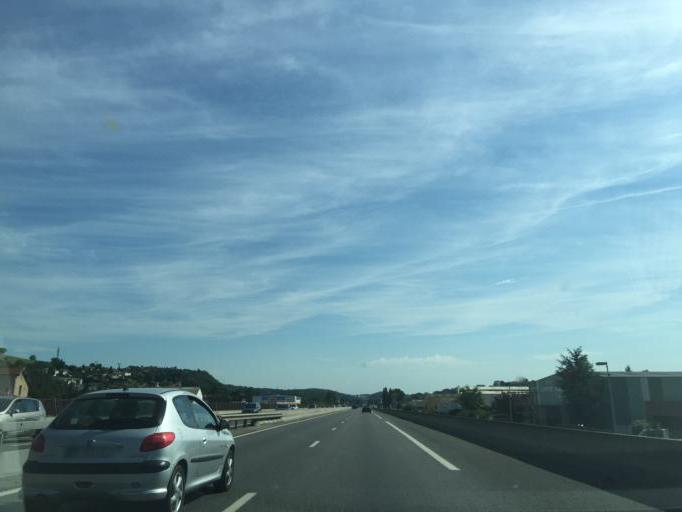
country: FR
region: Rhone-Alpes
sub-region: Departement de la Loire
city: La Grand-Croix
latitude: 45.4979
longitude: 4.5591
